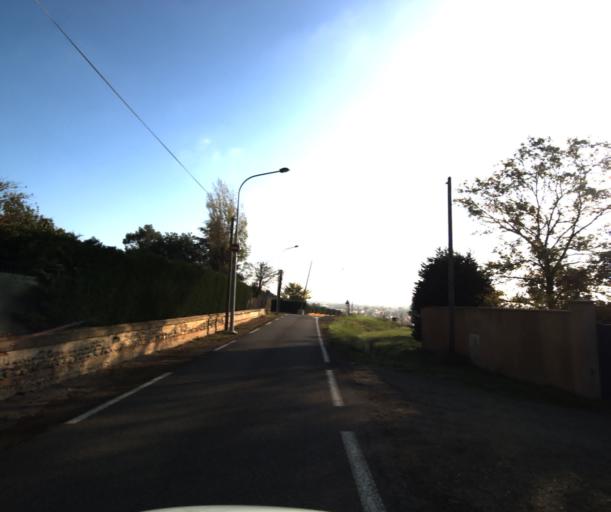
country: FR
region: Midi-Pyrenees
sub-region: Departement de la Haute-Garonne
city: Colomiers
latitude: 43.5947
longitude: 1.3381
